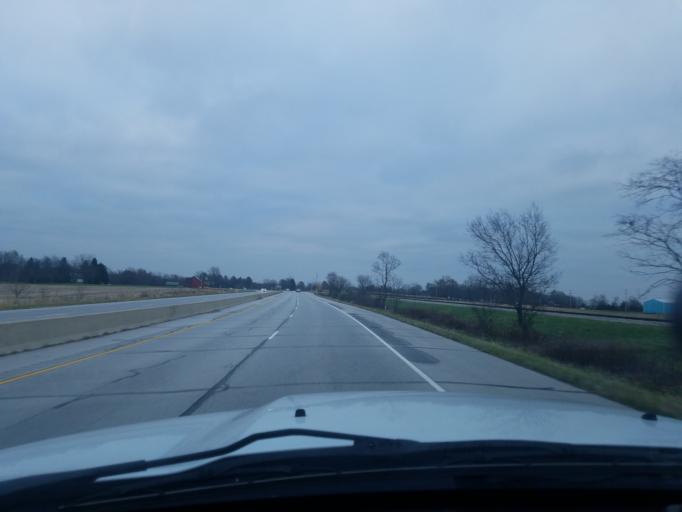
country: US
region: Indiana
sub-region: Delaware County
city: Yorktown
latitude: 40.2164
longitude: -85.5459
